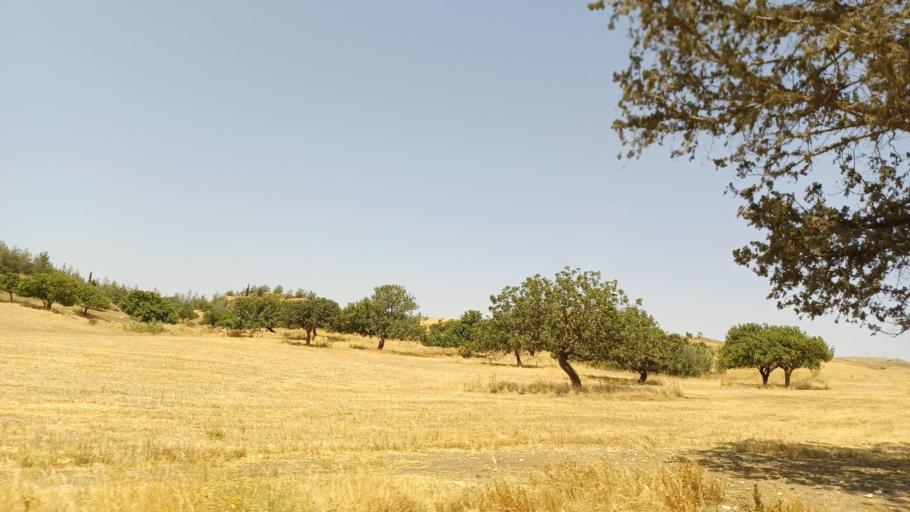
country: CY
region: Larnaka
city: Troulloi
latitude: 35.0210
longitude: 33.6363
